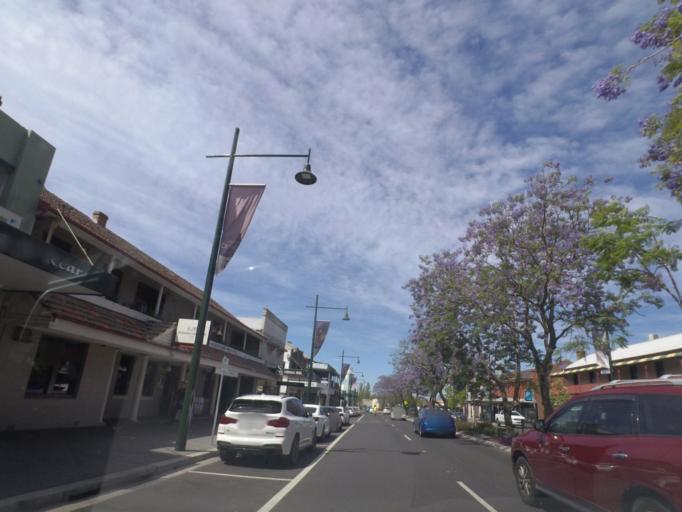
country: AU
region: New South Wales
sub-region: Camden
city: Elderslie
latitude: -34.0542
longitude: 150.6967
